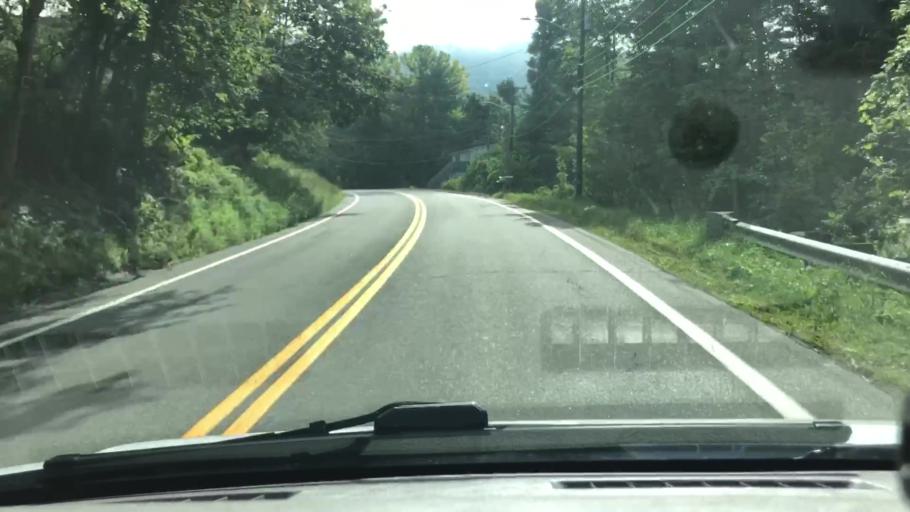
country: US
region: Massachusetts
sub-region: Berkshire County
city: North Adams
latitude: 42.6906
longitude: -73.0848
